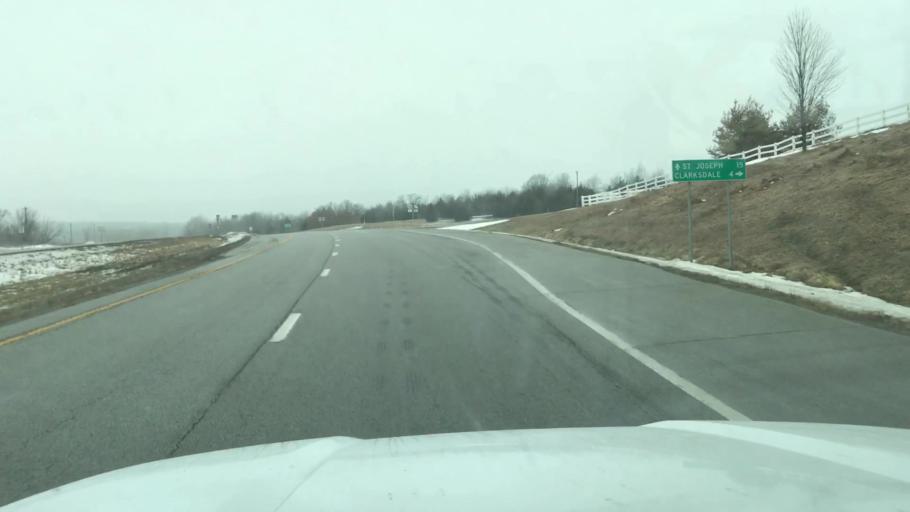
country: US
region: Missouri
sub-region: Clinton County
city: Gower
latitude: 39.7612
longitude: -94.5666
